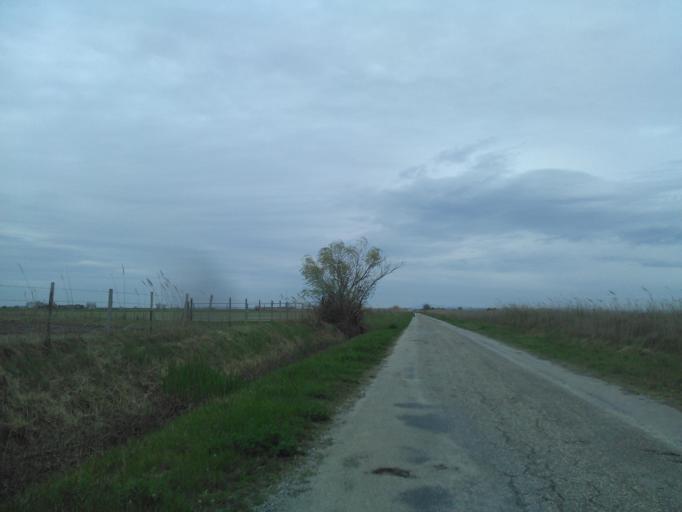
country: FR
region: Provence-Alpes-Cote d'Azur
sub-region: Departement des Bouches-du-Rhone
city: Arles
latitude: 43.6024
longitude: 4.5532
